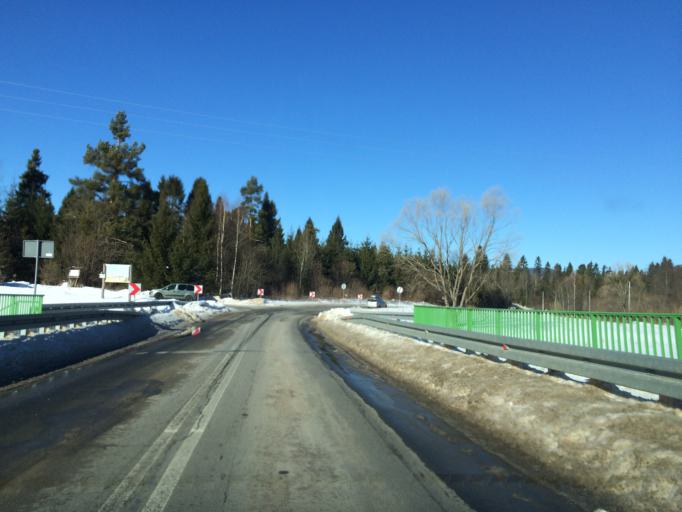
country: PL
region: Subcarpathian Voivodeship
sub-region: Powiat leski
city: Cisna
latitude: 49.1611
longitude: 22.4577
